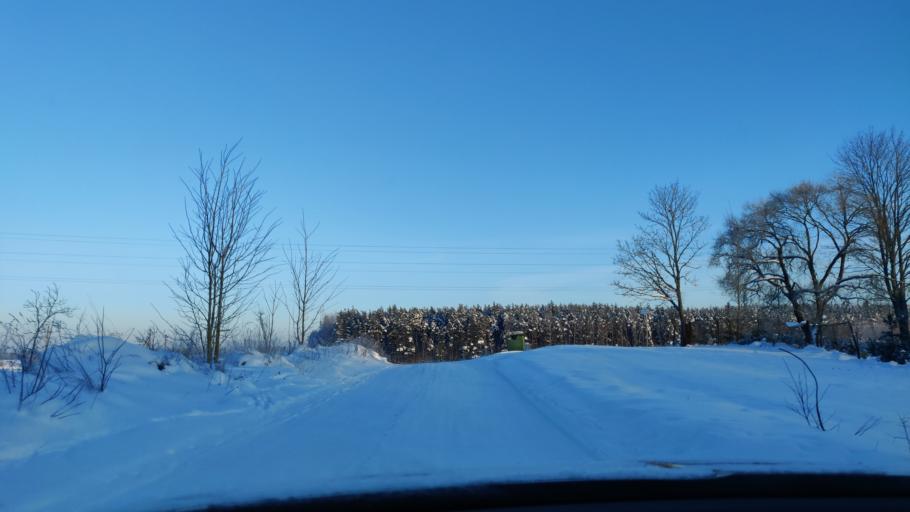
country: LT
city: Trakai
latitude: 54.6134
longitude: 24.9374
